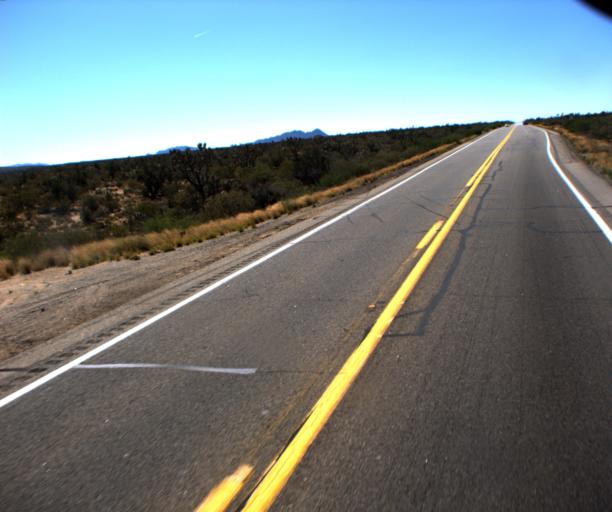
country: US
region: Arizona
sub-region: Yavapai County
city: Congress
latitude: 34.2904
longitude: -113.1104
